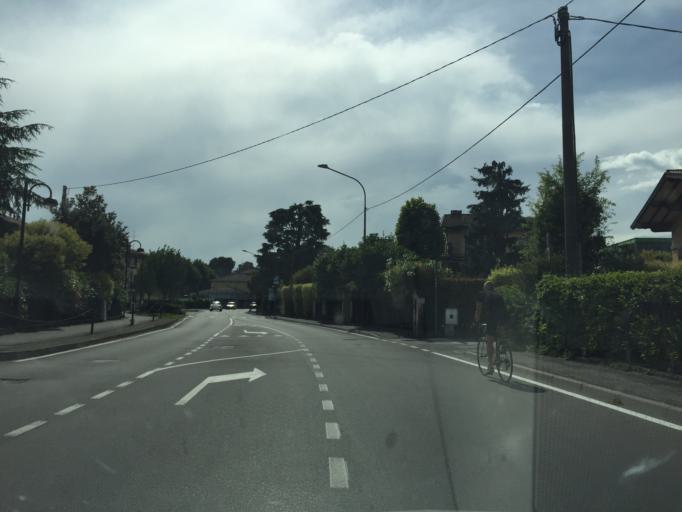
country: IT
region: Lombardy
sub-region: Provincia di Brescia
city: Poncarale
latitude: 45.4611
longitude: 10.1774
